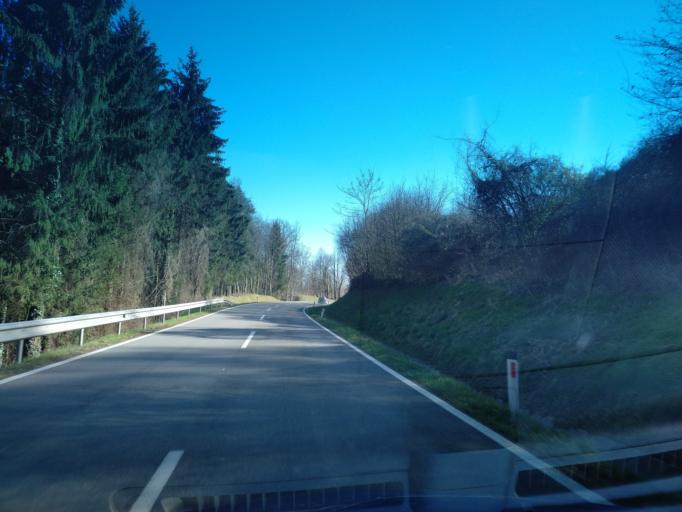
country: AT
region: Styria
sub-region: Politischer Bezirk Leibnitz
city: Stocking
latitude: 46.8733
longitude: 15.5299
